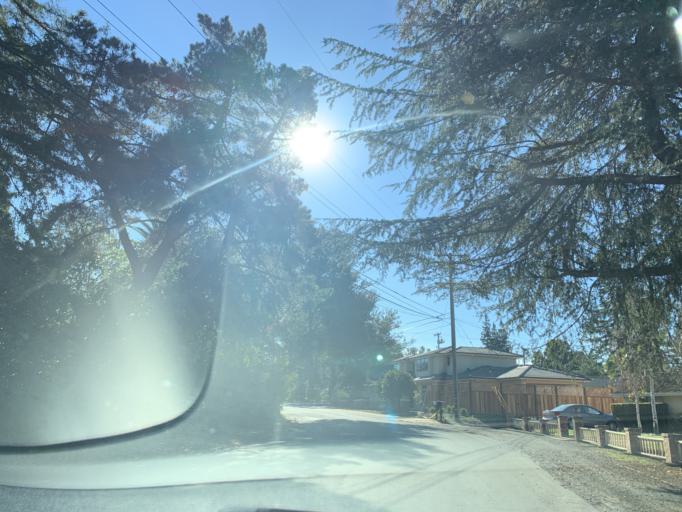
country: US
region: California
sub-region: Santa Clara County
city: Los Altos
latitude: 37.3859
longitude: -122.1055
